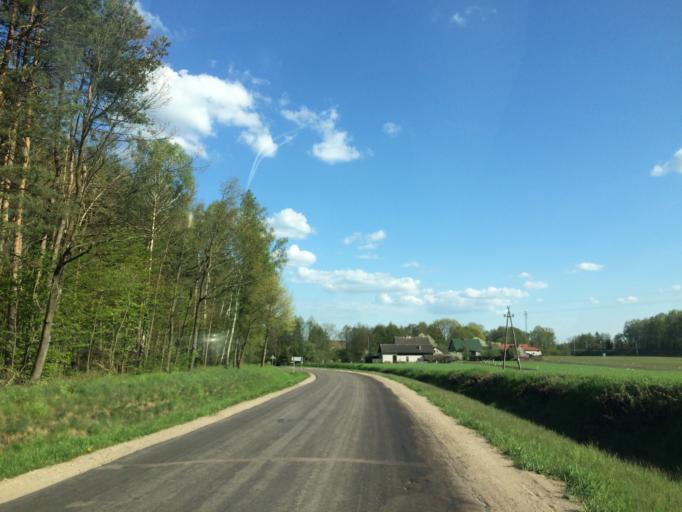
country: PL
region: Warmian-Masurian Voivodeship
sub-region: Powiat dzialdowski
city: Rybno
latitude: 53.3584
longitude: 19.9489
